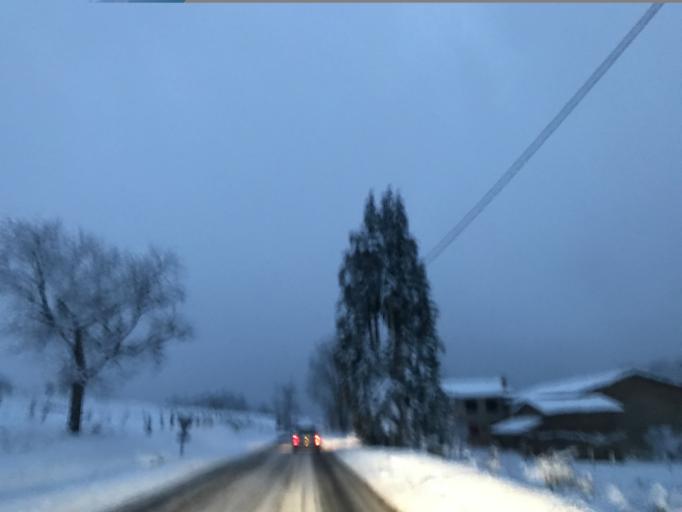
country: FR
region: Auvergne
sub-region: Departement du Puy-de-Dome
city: Courpiere
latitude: 45.7177
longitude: 3.5901
